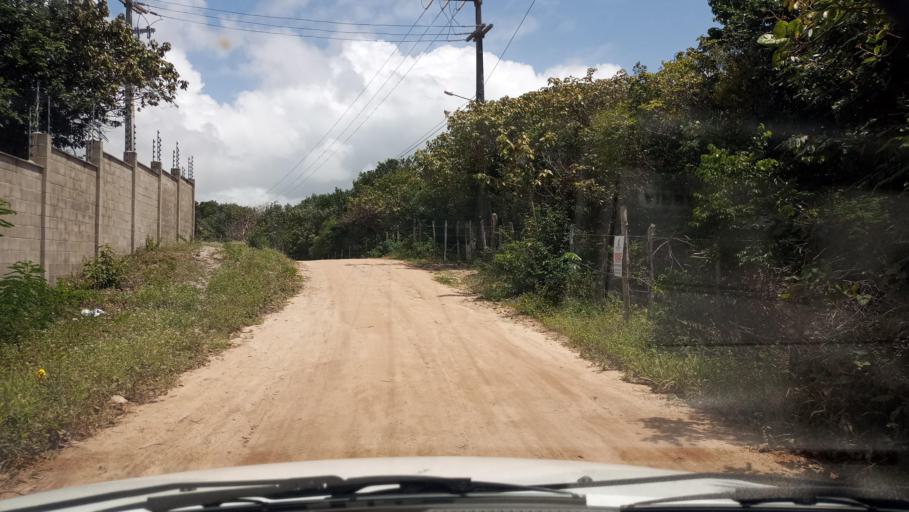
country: BR
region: Rio Grande do Norte
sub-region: Ares
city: Ares
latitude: -6.2456
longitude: -35.0441
